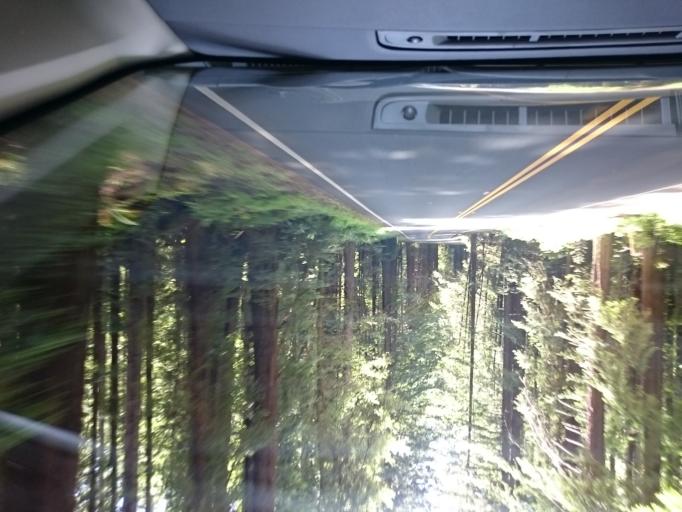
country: US
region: California
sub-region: Mendocino County
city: Boonville
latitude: 39.1559
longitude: -123.6240
